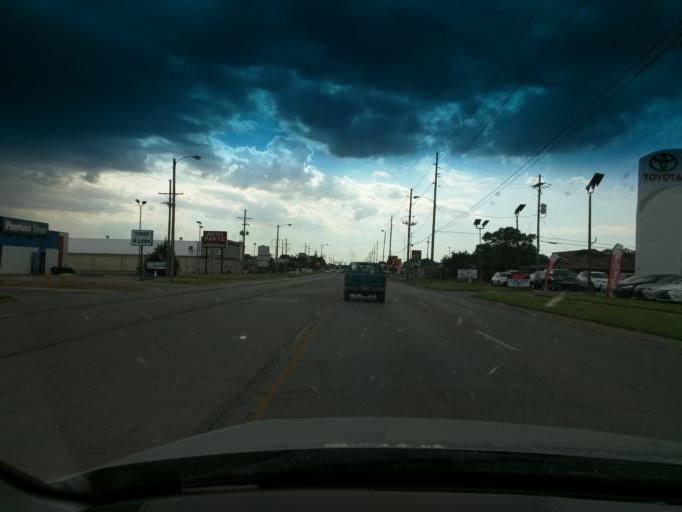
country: US
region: Kansas
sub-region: Reno County
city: Hutchinson
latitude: 38.0866
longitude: -97.9084
